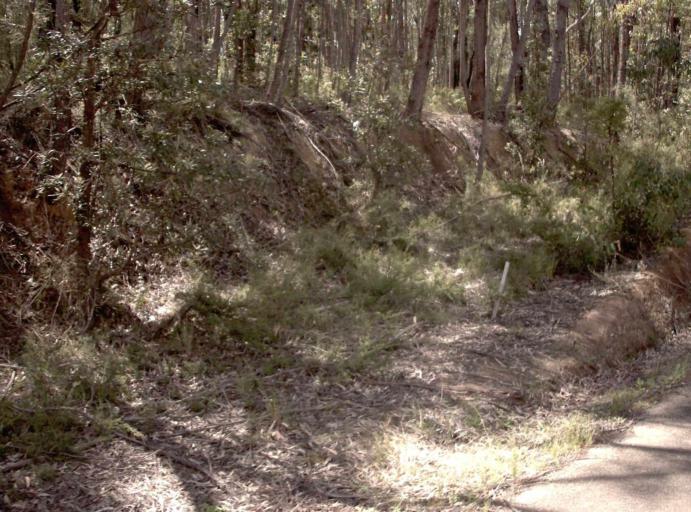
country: AU
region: New South Wales
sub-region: Bombala
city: Bombala
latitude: -37.5733
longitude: 149.3147
